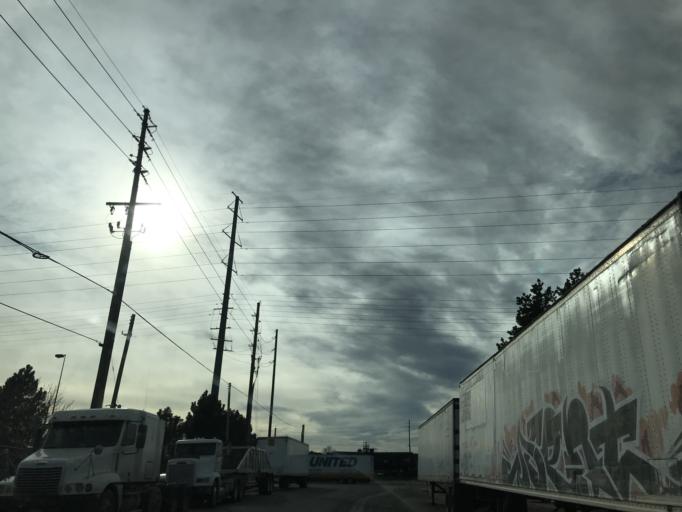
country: US
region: Colorado
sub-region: Adams County
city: Commerce City
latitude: 39.7742
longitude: -104.9082
